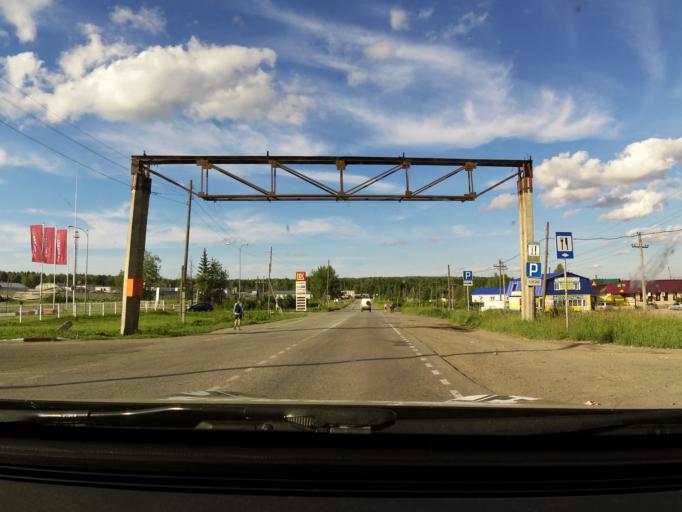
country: RU
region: Kirov
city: Omutninsk
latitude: 58.6947
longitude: 52.2193
